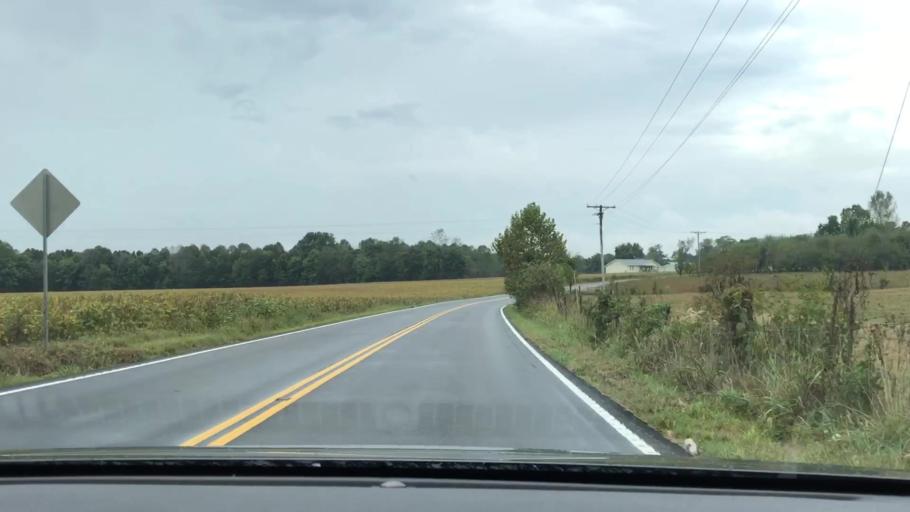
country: US
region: Tennessee
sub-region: Macon County
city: Red Boiling Springs
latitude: 36.5081
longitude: -85.8620
